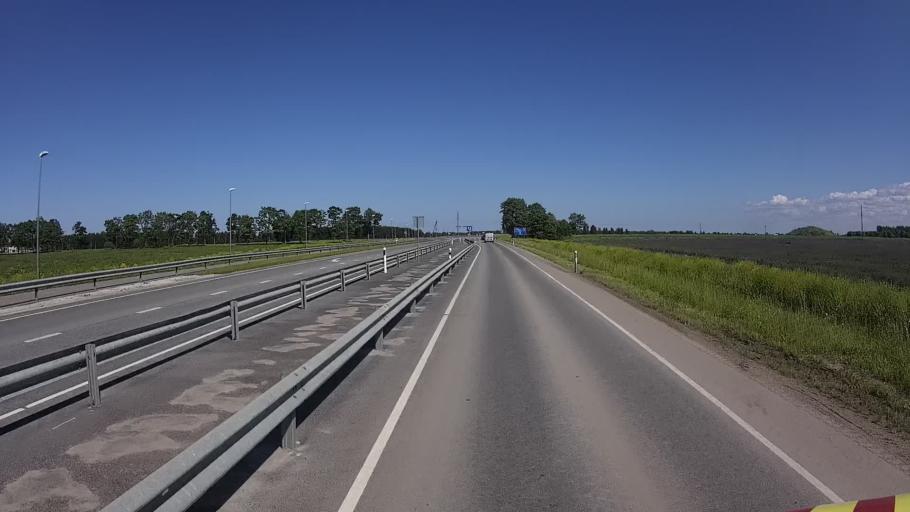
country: EE
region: Ida-Virumaa
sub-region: Kohtla-Jaerve linn
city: Kohtla-Jarve
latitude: 59.4032
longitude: 27.3072
